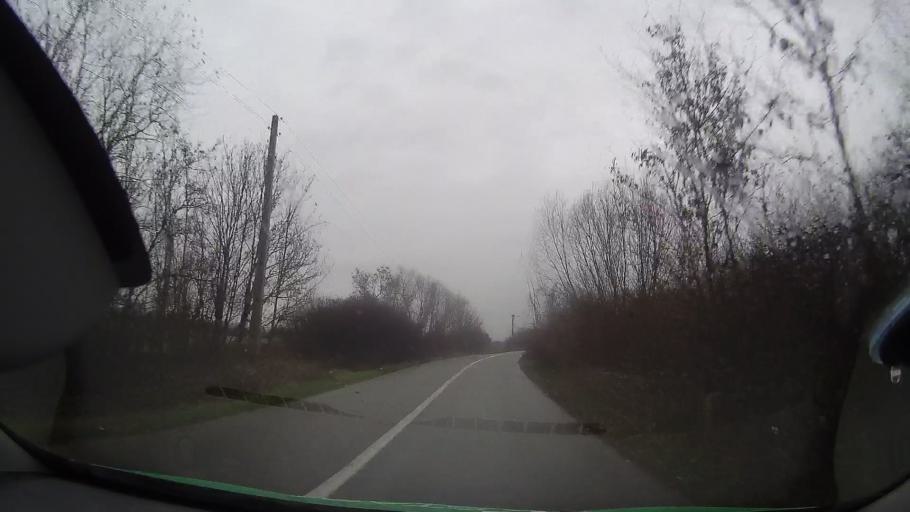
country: RO
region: Bihor
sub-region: Comuna Tinca
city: Tinca
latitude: 46.7408
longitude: 21.9533
